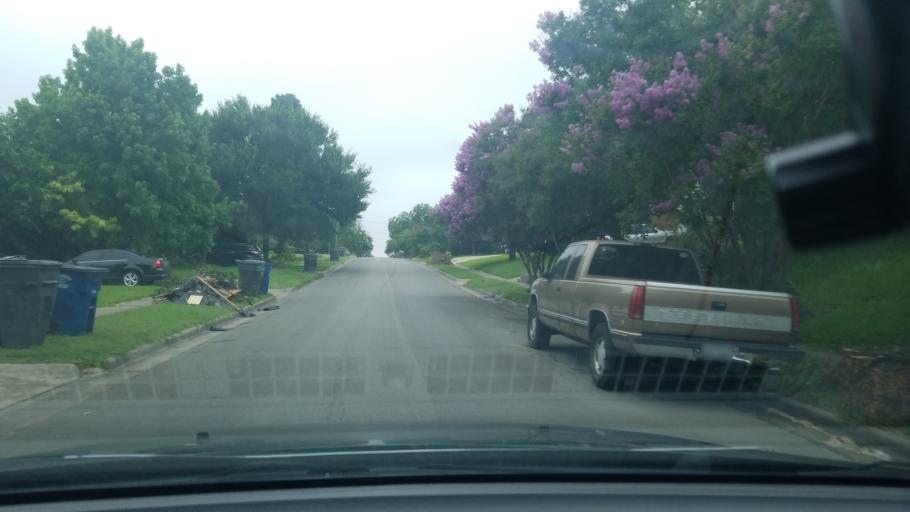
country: US
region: Texas
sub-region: Dallas County
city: Balch Springs
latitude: 32.7561
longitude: -96.6933
